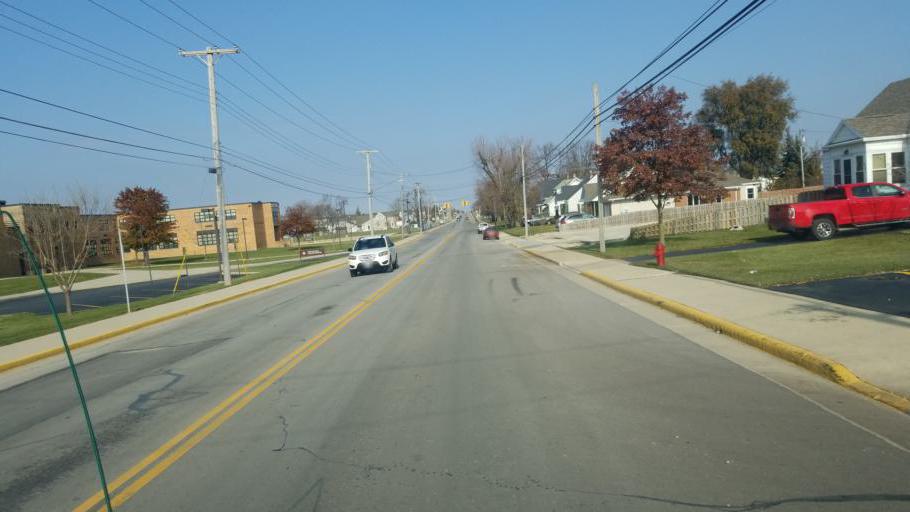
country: US
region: Ohio
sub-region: Mercer County
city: Coldwater
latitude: 40.4820
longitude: -84.6287
